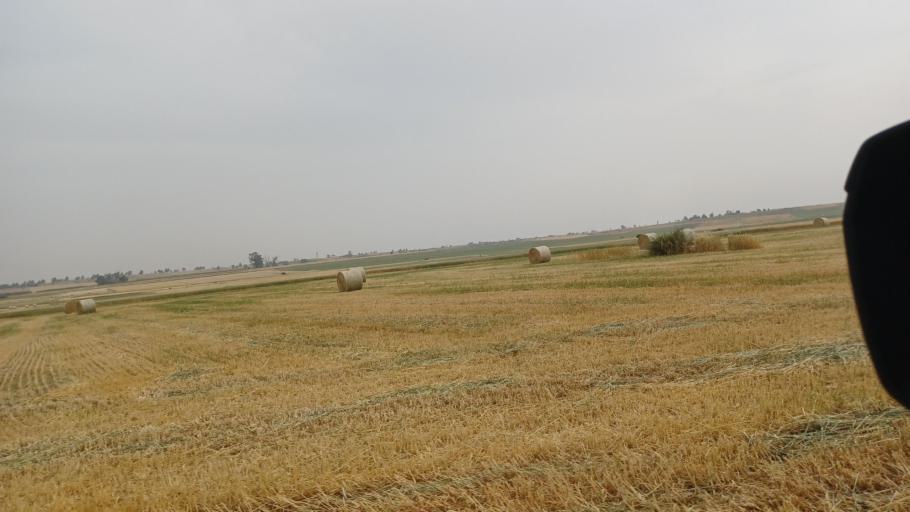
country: CY
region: Lefkosia
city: Mammari
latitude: 35.1704
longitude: 33.2309
